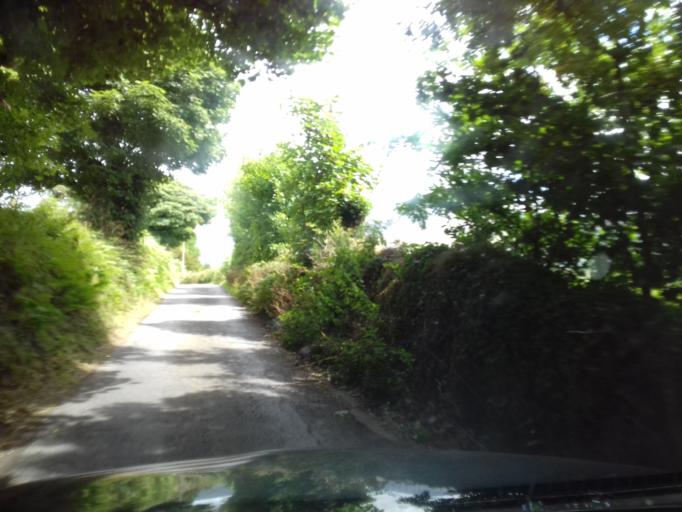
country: IE
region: Leinster
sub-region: Kilkenny
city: Graiguenamanagh
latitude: 52.6212
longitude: -6.8375
